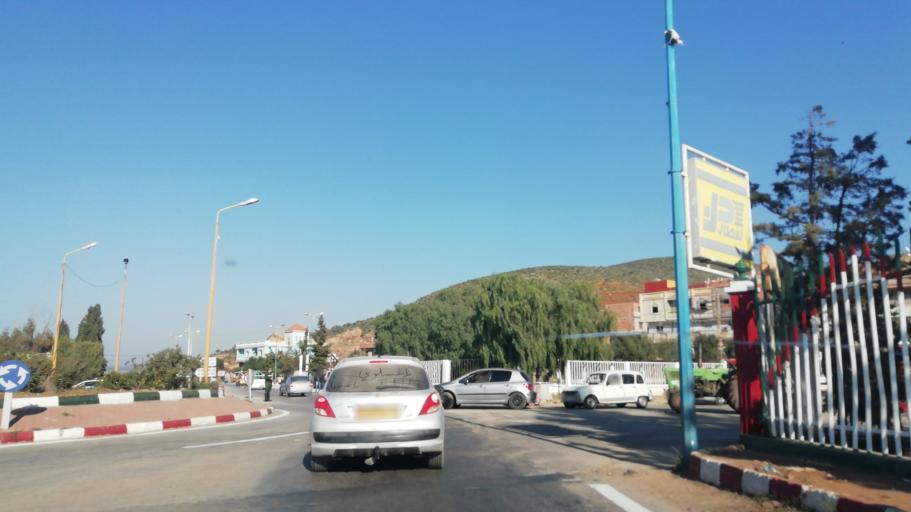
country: DZ
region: Tlemcen
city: Remchi
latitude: 35.1511
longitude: -1.4527
